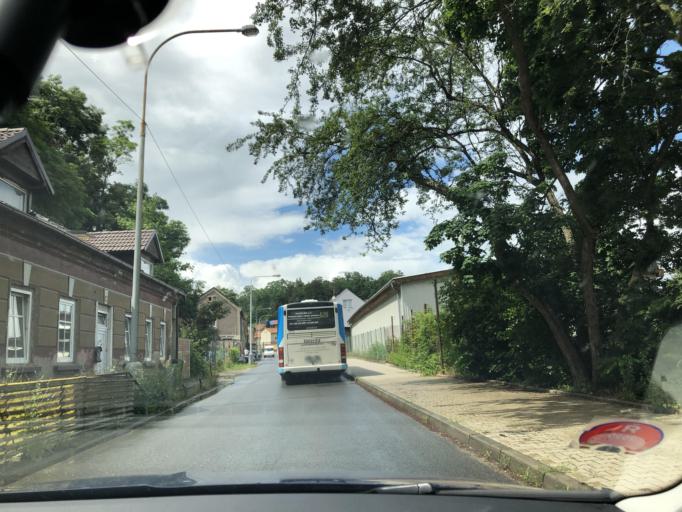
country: CZ
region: Central Bohemia
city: Kralupy nad Vltavou
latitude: 50.2437
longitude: 14.3050
